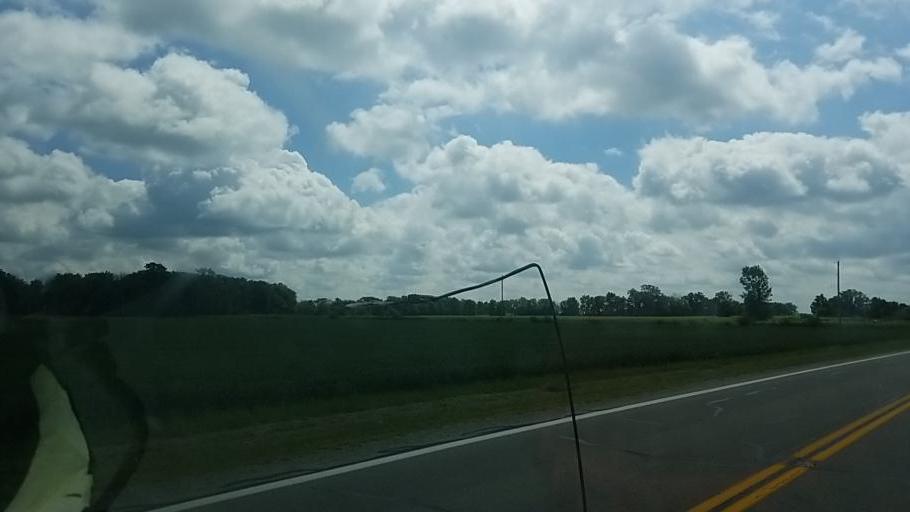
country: US
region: Ohio
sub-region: Madison County
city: Bethel
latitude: 39.6932
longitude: -83.4547
